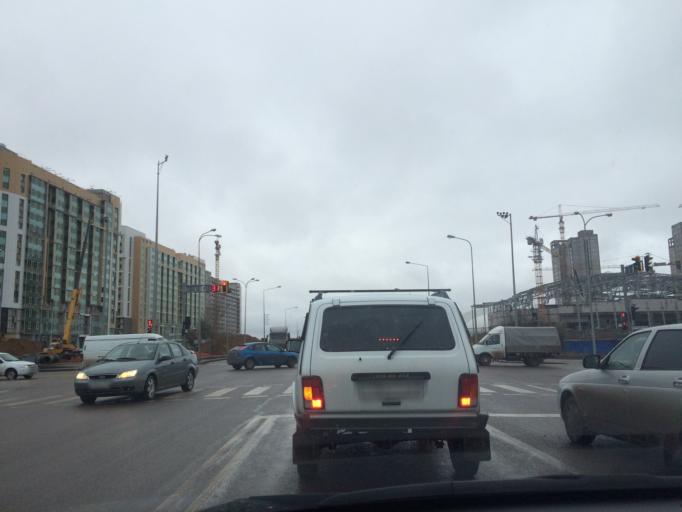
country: KZ
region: Astana Qalasy
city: Astana
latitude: 51.1165
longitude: 71.4115
